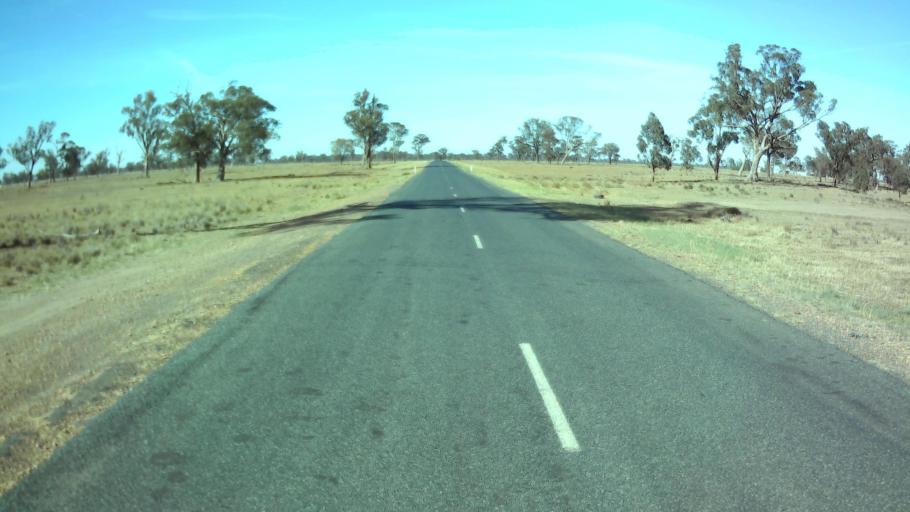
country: AU
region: New South Wales
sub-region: Weddin
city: Grenfell
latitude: -34.0446
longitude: 147.9261
